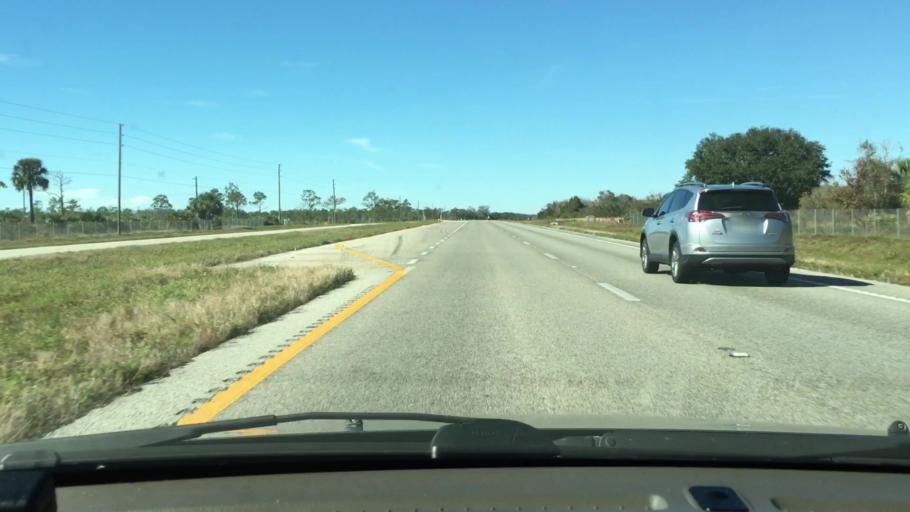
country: US
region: Florida
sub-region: Osceola County
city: Saint Cloud
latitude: 28.1314
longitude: -81.0085
